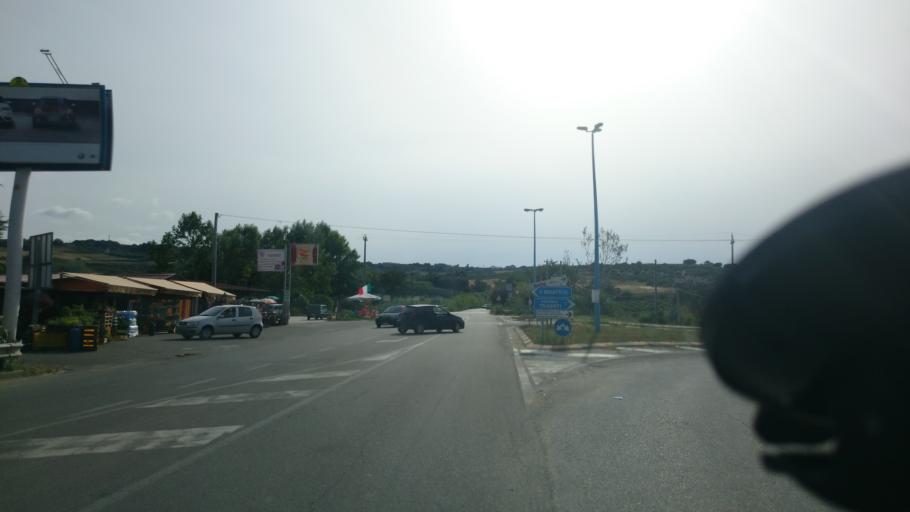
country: IT
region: Calabria
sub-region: Provincia di Vibo-Valentia
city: Pannaconi
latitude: 38.7095
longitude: 16.0718
